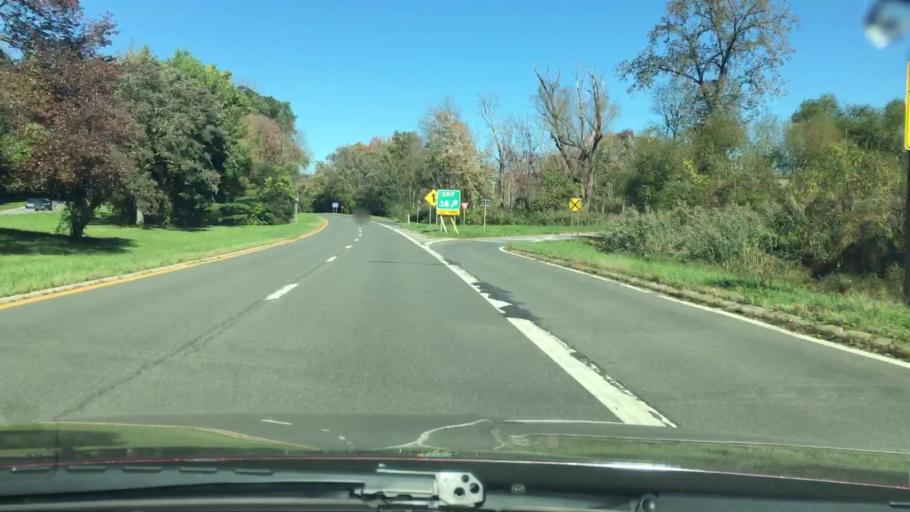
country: US
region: New York
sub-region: Westchester County
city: Mount Kisco
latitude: 41.2267
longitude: -73.7178
